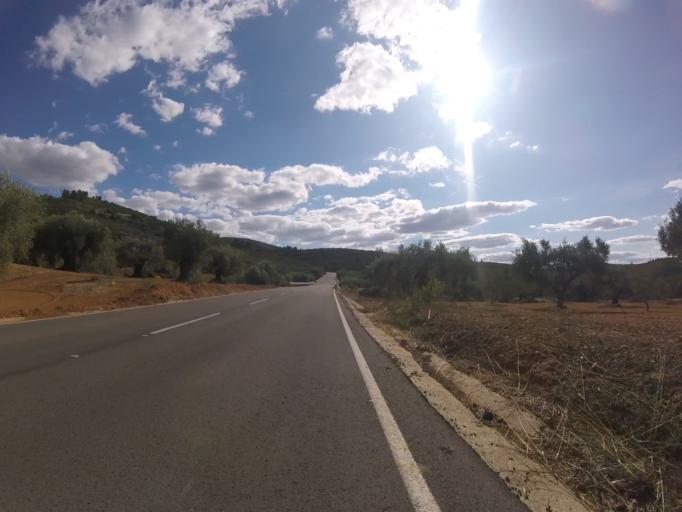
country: ES
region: Valencia
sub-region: Provincia de Castello
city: Cuevas de Vinroma
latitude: 40.2997
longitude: 0.1677
